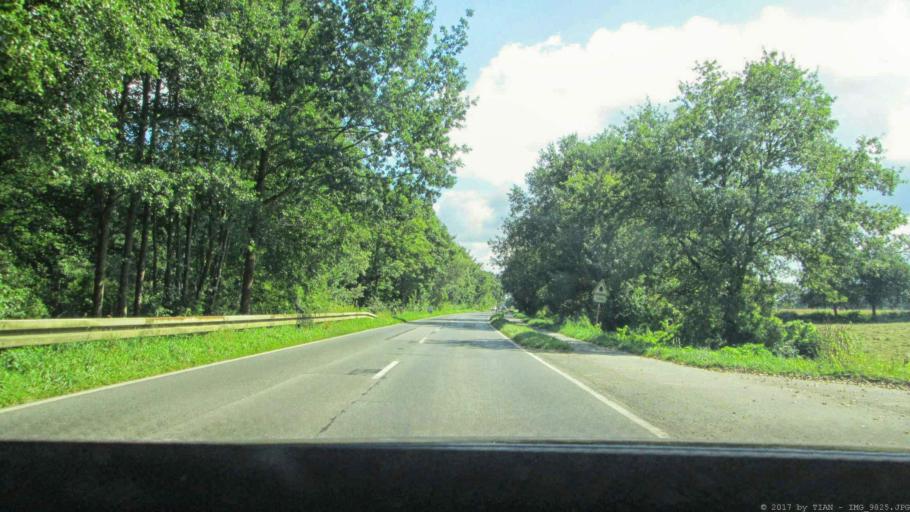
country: DE
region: Schleswig-Holstein
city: Jersbek
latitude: 53.7384
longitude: 10.2295
